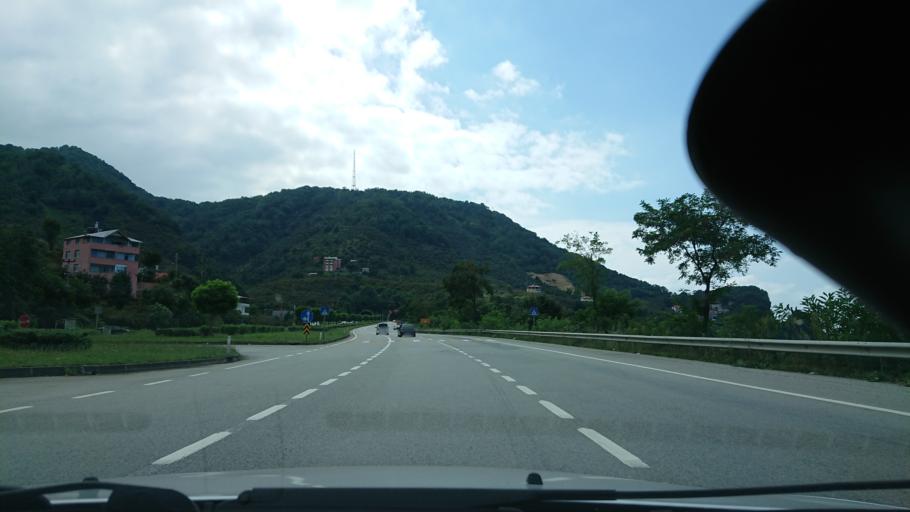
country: TR
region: Trabzon
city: Espiye
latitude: 40.9709
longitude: 38.6370
